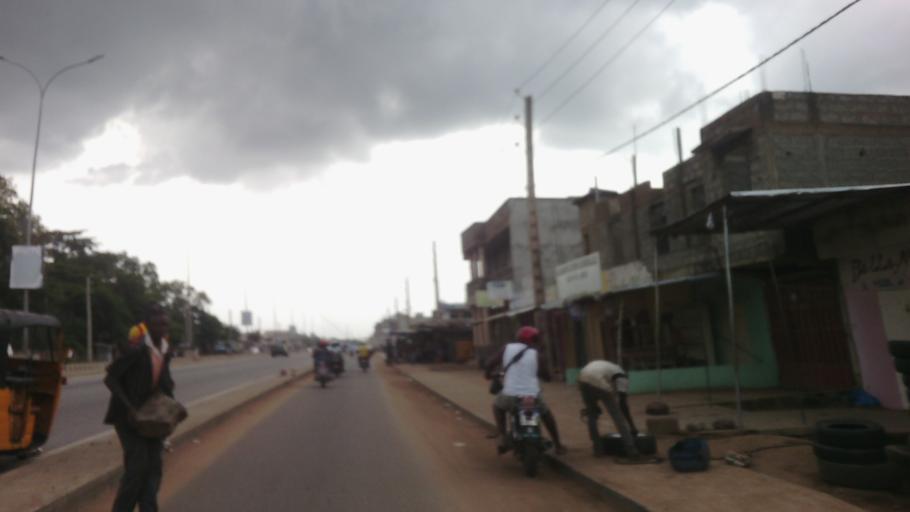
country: BJ
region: Atlantique
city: Abomey-Calavi
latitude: 6.4647
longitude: 2.3560
